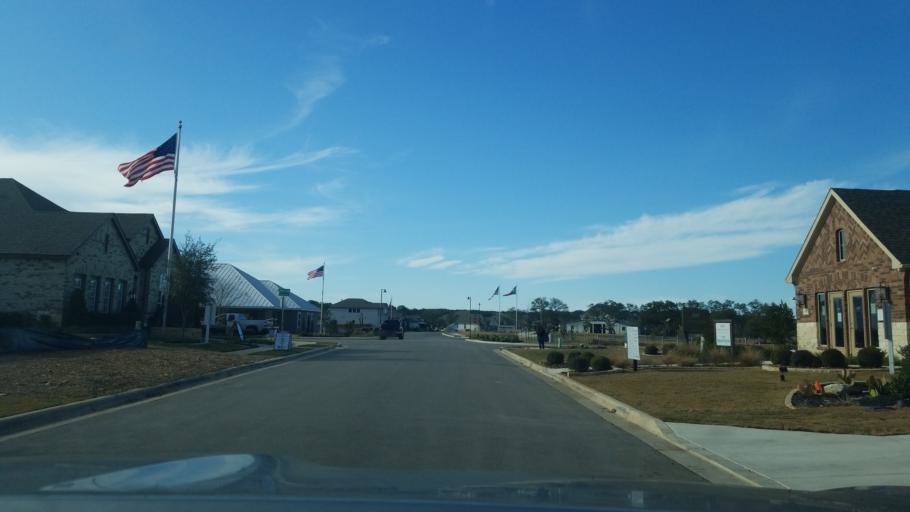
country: US
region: Texas
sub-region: Comal County
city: Canyon Lake
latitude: 29.7768
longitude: -98.2864
